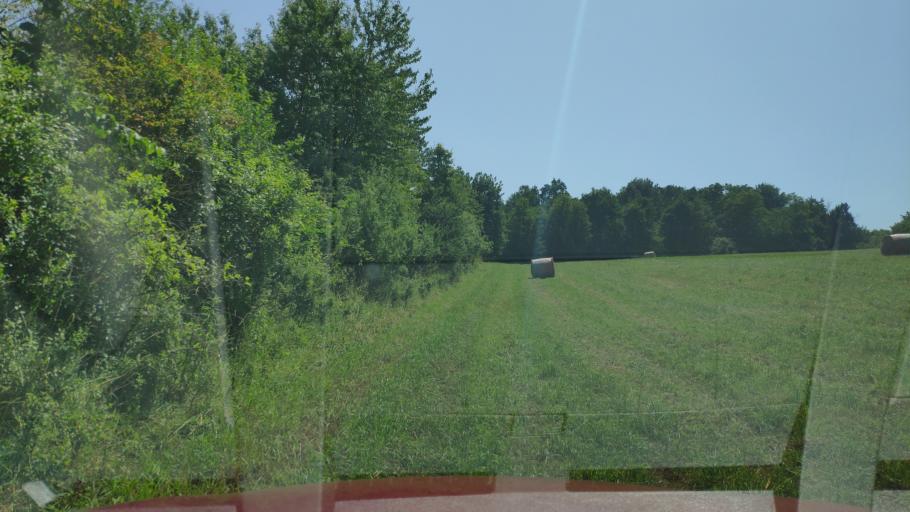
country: SK
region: Presovsky
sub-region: Okres Presov
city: Presov
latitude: 48.9413
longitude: 21.1709
